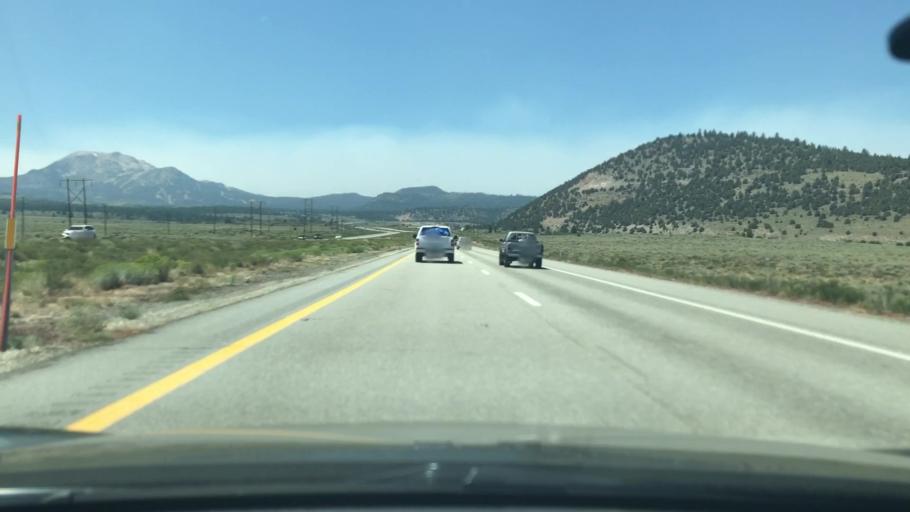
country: US
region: California
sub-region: Mono County
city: Mammoth Lakes
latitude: 37.6339
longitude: -118.8785
